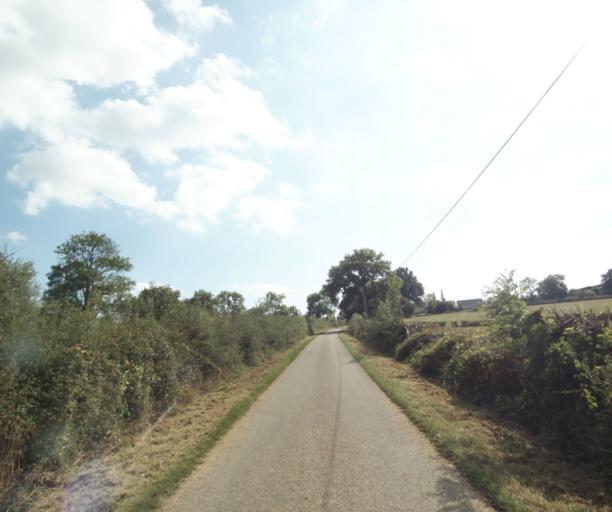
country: FR
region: Bourgogne
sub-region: Departement de Saone-et-Loire
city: Charolles
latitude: 46.4670
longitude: 4.2268
